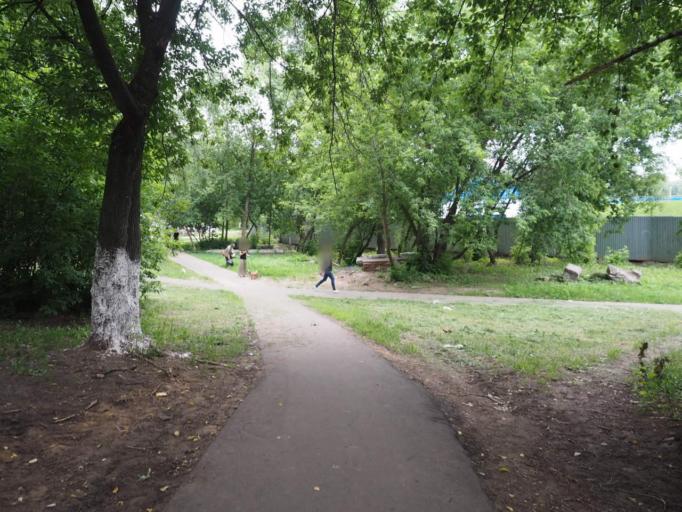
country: RU
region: Moskovskaya
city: Lyubertsy
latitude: 55.6606
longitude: 37.9000
